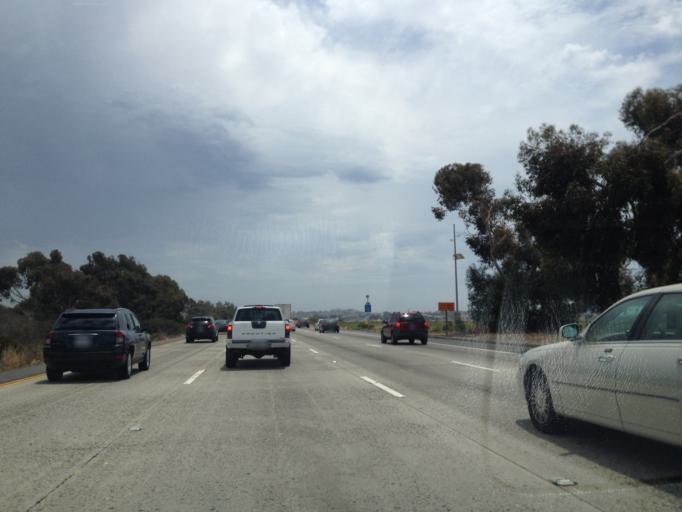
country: US
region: California
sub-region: San Diego County
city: Camp Pendleton South
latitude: 33.2400
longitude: -117.4129
